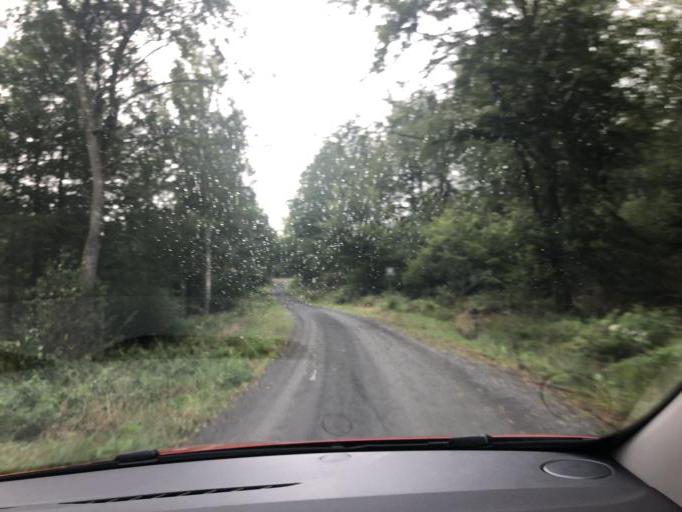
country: SE
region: Blekinge
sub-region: Solvesborgs Kommun
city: Soelvesborg
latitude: 56.1403
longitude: 14.5847
